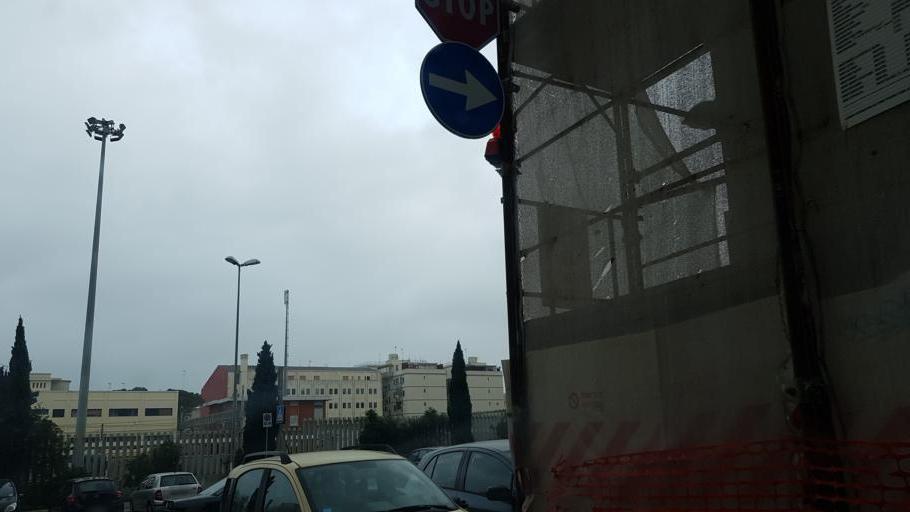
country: IT
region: Apulia
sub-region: Provincia di Brindisi
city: Brindisi
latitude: 40.6332
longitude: 17.9384
